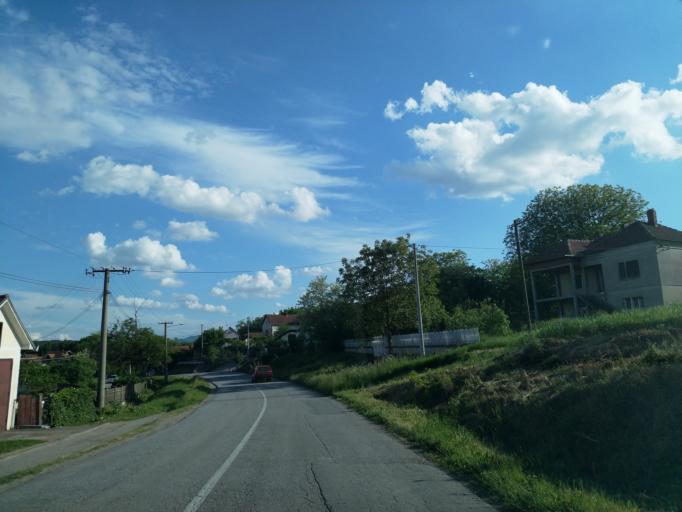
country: RS
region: Central Serbia
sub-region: Sumadijski Okrug
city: Batocina
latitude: 44.1536
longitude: 21.1027
